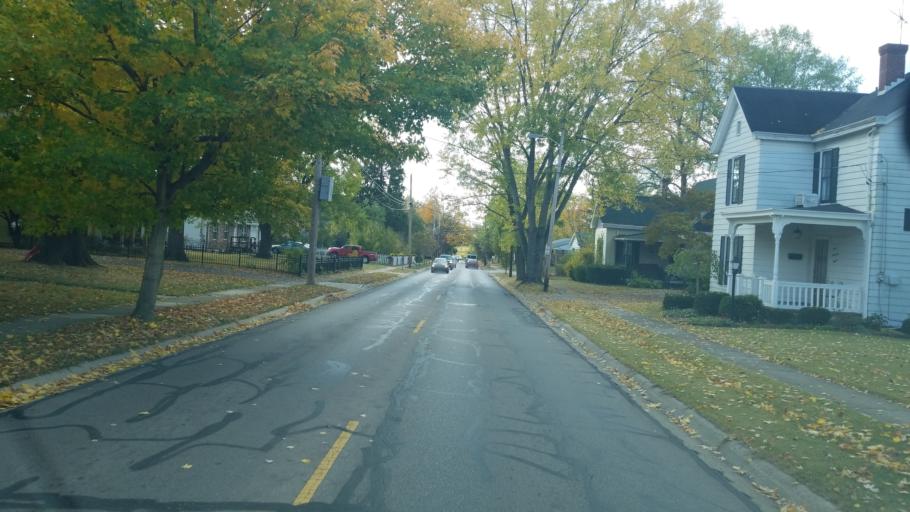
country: US
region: Ohio
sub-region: Warren County
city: Lebanon
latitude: 39.4357
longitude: -84.1988
